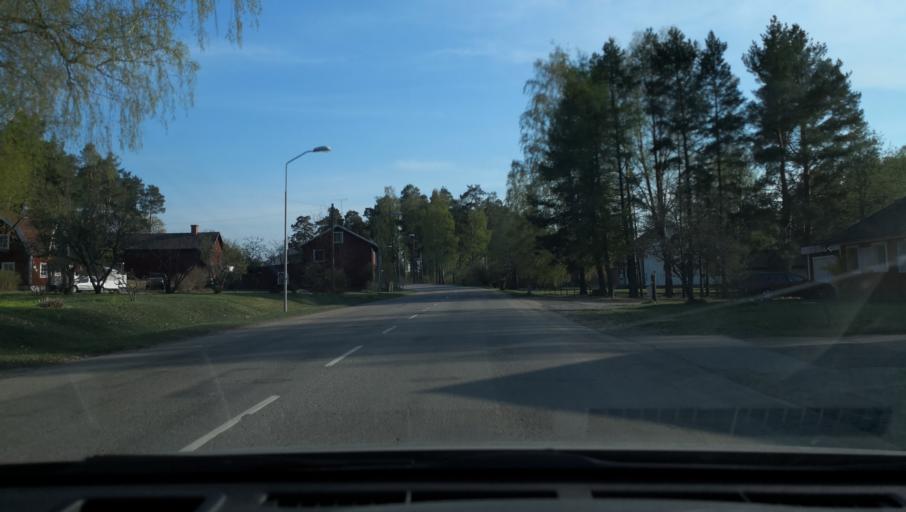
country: SE
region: Uppsala
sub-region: Heby Kommun
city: Tarnsjo
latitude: 60.1658
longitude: 16.9382
